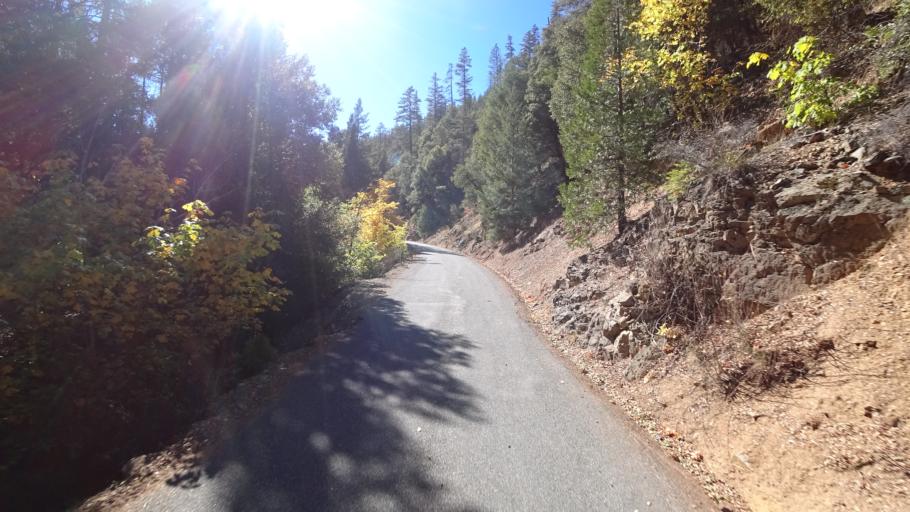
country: US
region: California
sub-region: Siskiyou County
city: Happy Camp
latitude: 41.3407
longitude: -123.0448
